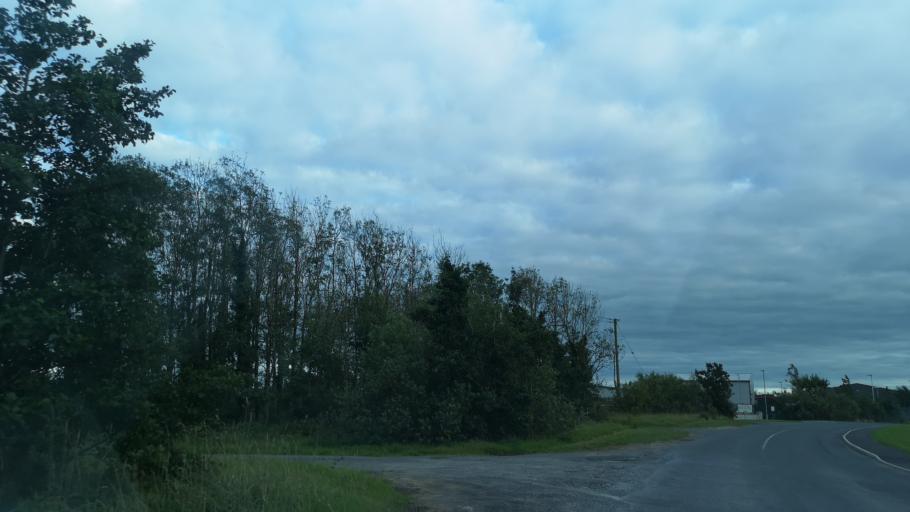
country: IE
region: Connaught
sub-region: County Galway
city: Athenry
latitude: 53.2887
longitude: -8.7552
